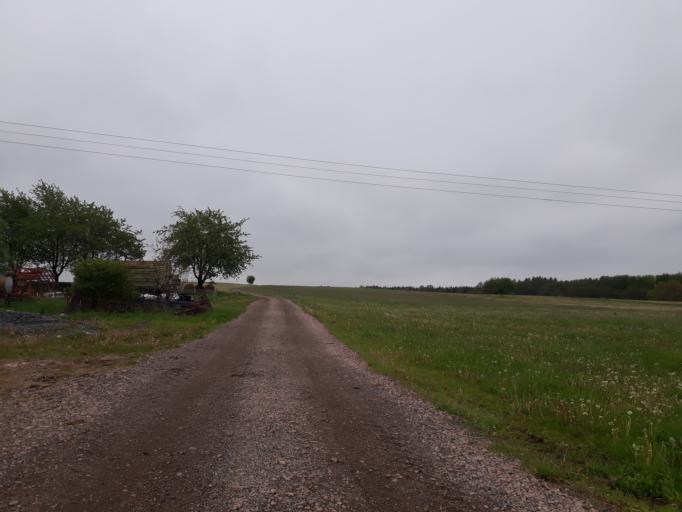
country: DE
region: Saxony
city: Reinhardtsgrimma
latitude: 50.8895
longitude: 13.7533
